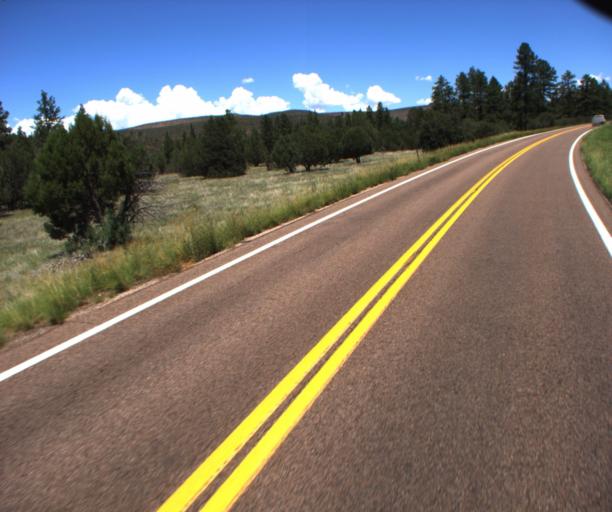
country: US
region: Arizona
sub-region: Navajo County
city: Linden
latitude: 34.0757
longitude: -110.1930
